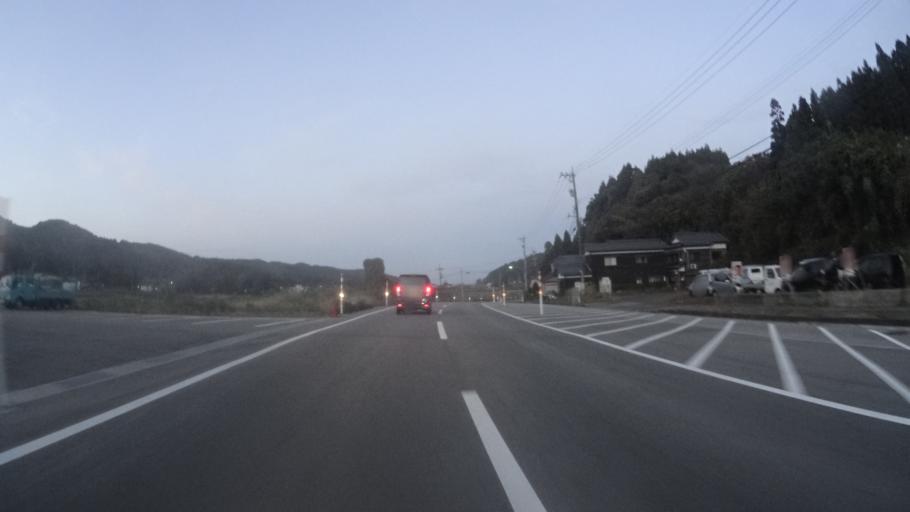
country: JP
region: Ishikawa
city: Nanao
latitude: 37.3670
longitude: 136.8706
